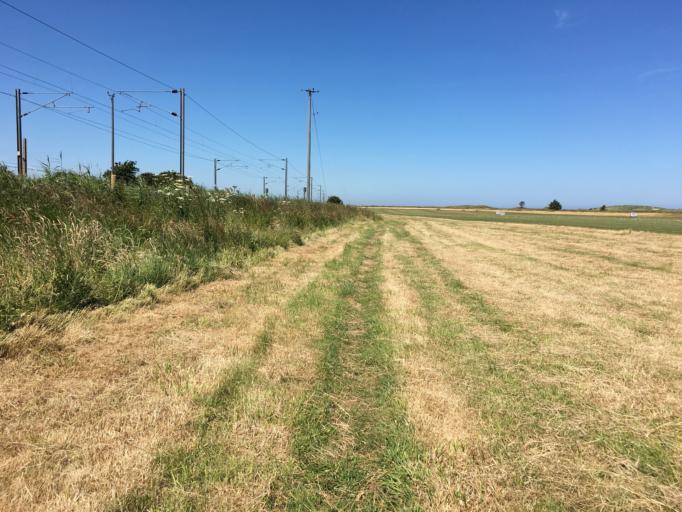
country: GB
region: England
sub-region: Northumberland
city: Ancroft
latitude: 55.7066
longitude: -1.9285
